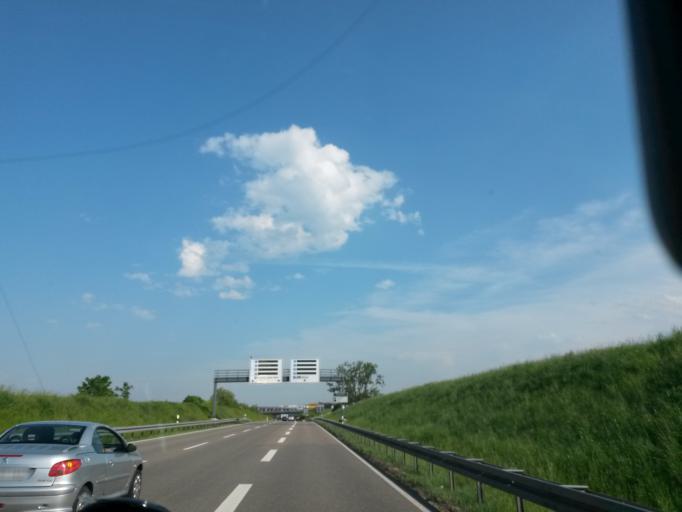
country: DE
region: Baden-Wuerttemberg
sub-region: Regierungsbezirk Stuttgart
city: Leinfelden-Echterdingen
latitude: 48.7004
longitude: 9.1810
